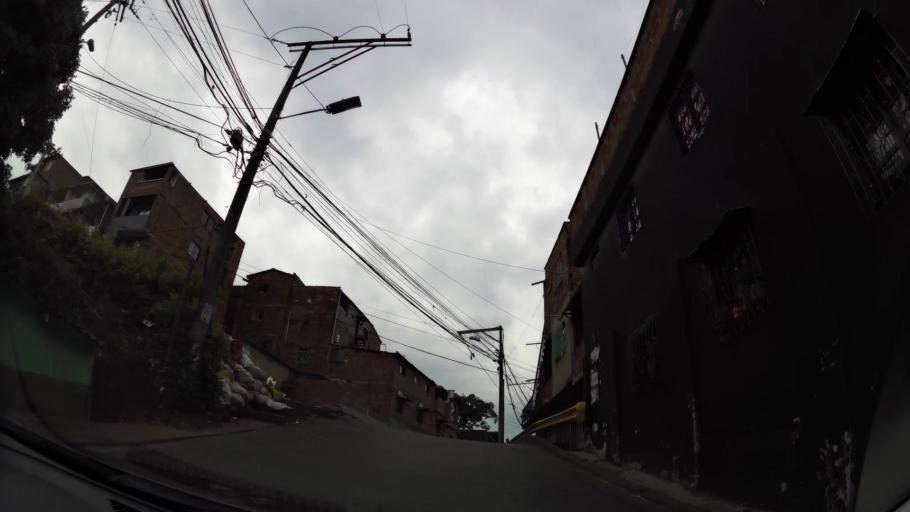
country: CO
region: Antioquia
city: Bello
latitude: 6.2944
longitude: -75.5521
